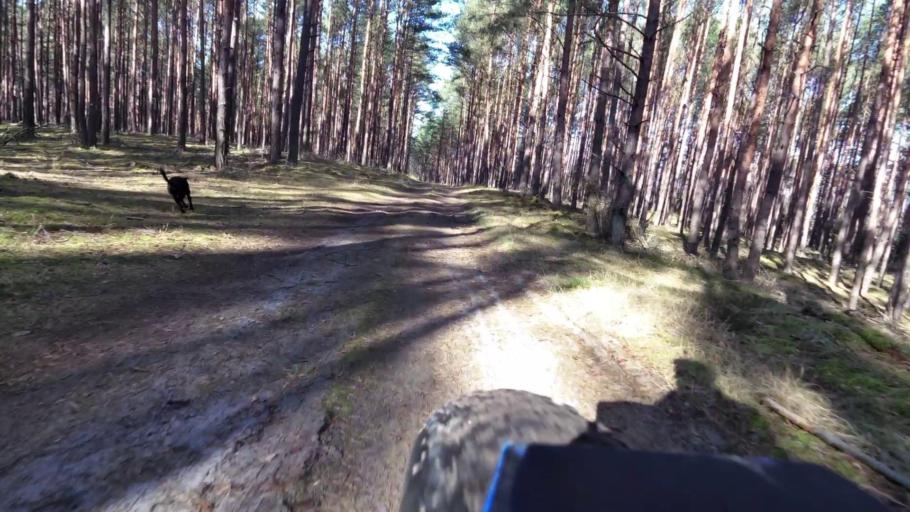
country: PL
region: Lubusz
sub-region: Powiat sulecinski
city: Torzym
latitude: 52.2207
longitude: 14.9858
